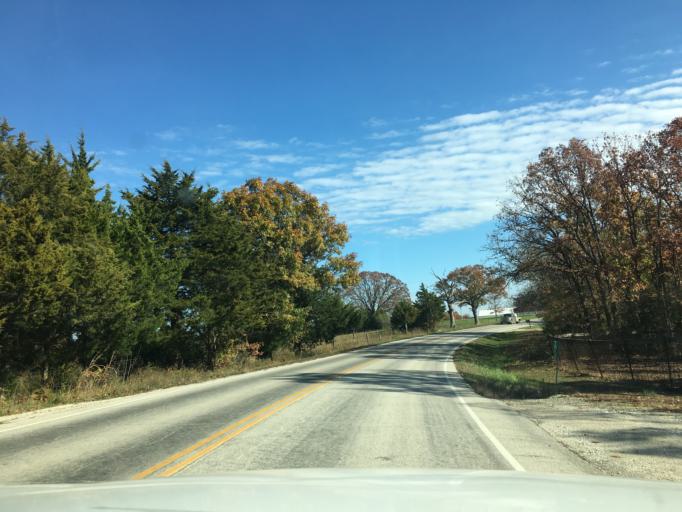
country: US
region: Missouri
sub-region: Maries County
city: Belle
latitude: 38.3039
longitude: -91.7290
